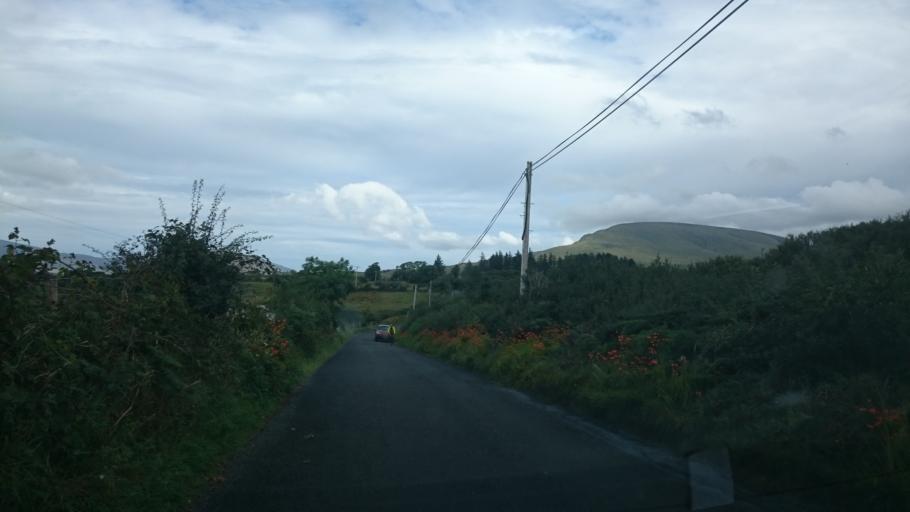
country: IE
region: Connaught
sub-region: Maigh Eo
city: Westport
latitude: 53.9096
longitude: -9.5529
